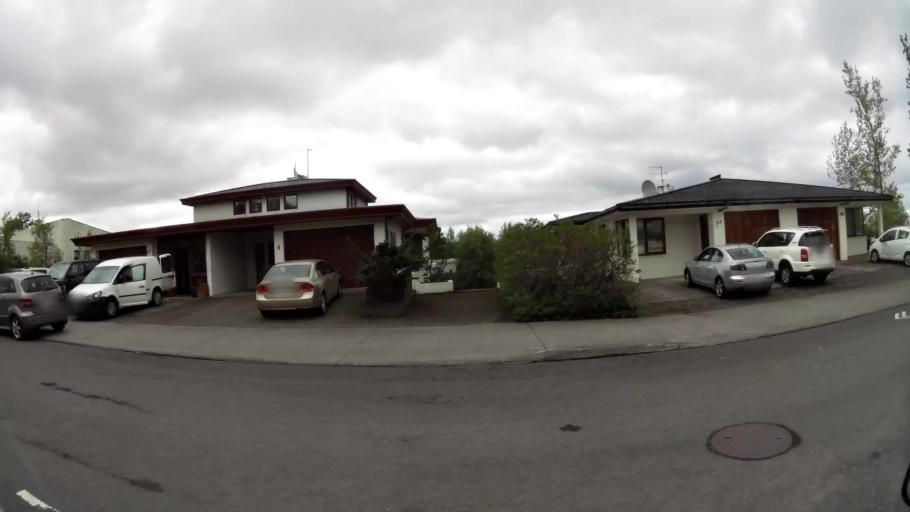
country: IS
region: Capital Region
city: Reykjavik
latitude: 64.1461
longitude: -21.8731
